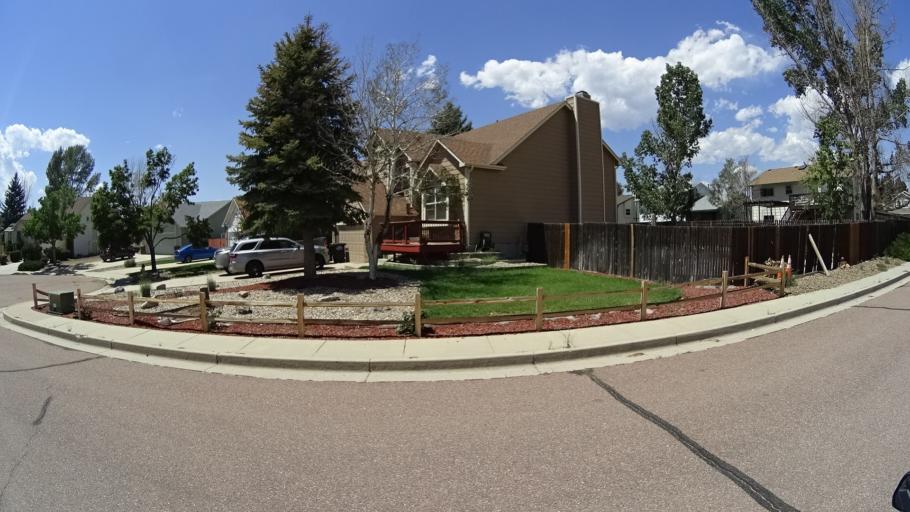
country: US
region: Colorado
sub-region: El Paso County
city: Black Forest
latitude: 38.9513
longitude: -104.7450
